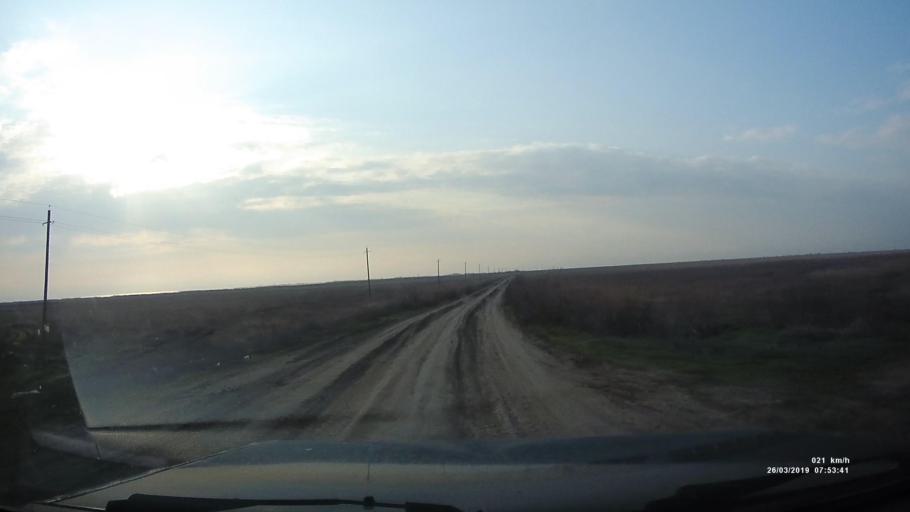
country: RU
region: Krasnodarskiy
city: Shabel'skoye
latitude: 47.1350
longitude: 38.5492
